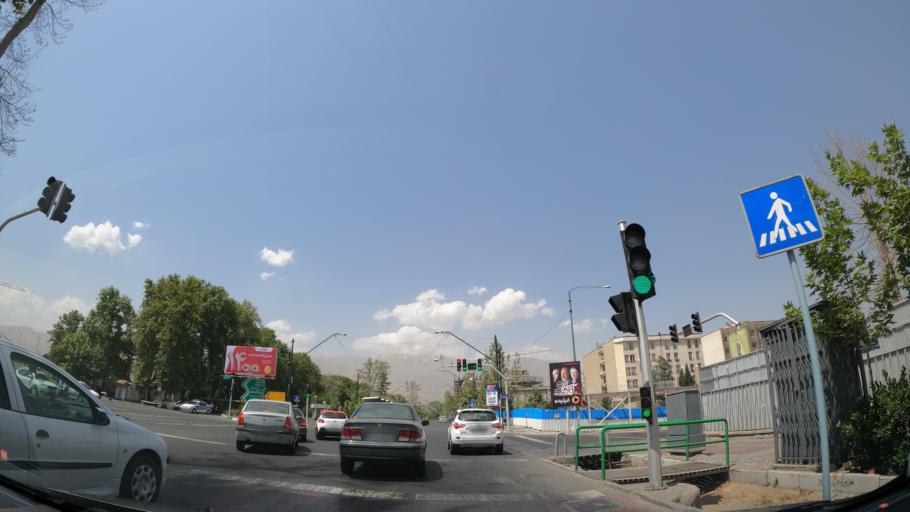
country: IR
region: Tehran
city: Tajrish
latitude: 35.7714
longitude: 51.4120
